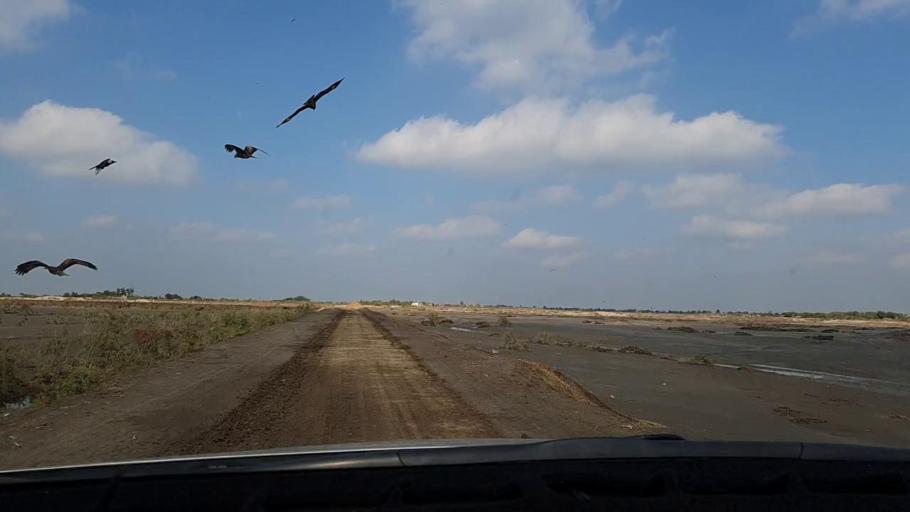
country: PK
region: Sindh
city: Tando Mittha Khan
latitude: 25.7650
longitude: 69.2684
